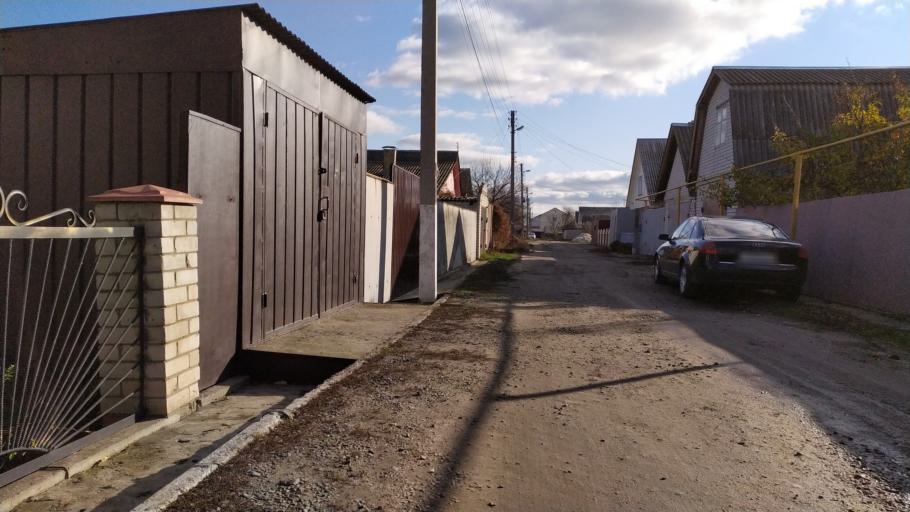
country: RU
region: Kursk
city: Kursk
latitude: 51.6468
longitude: 36.1543
